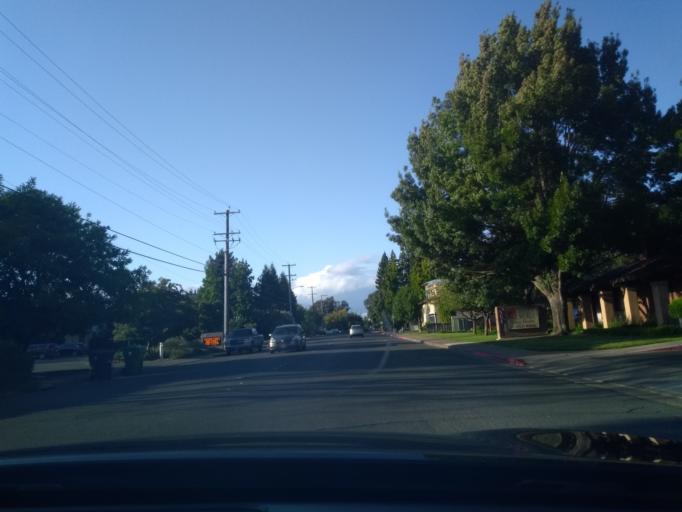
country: US
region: California
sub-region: Mendocino County
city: Ukiah
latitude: 39.1466
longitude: -123.1987
